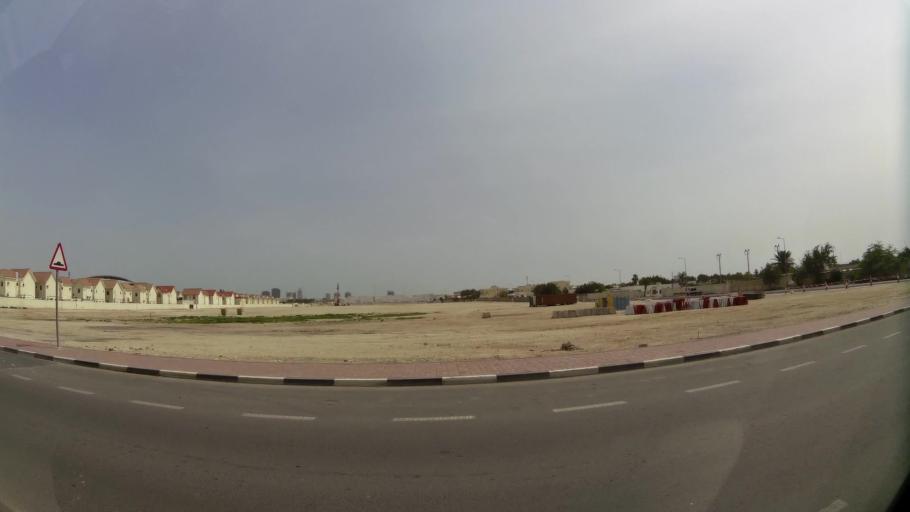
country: QA
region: Baladiyat ad Dawhah
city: Doha
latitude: 25.2653
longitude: 51.4872
